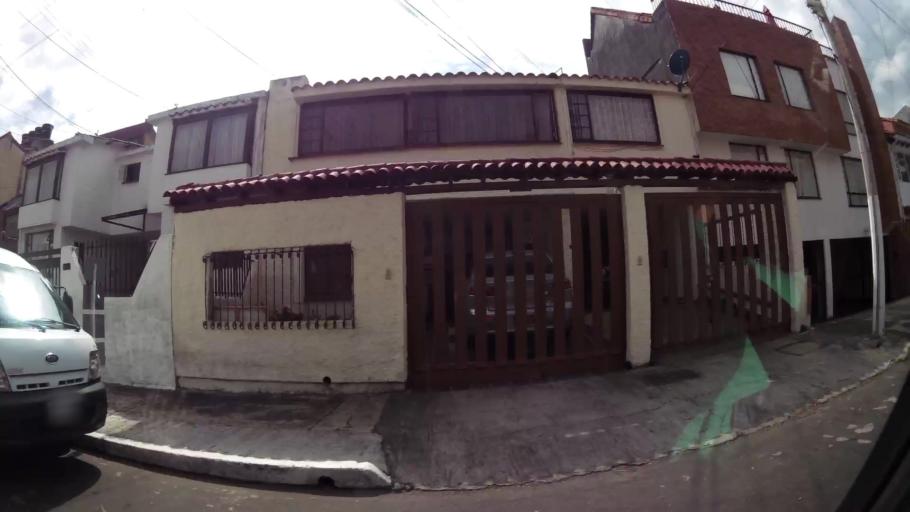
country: CO
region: Cundinamarca
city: La Calera
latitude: 4.7272
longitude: -74.0275
